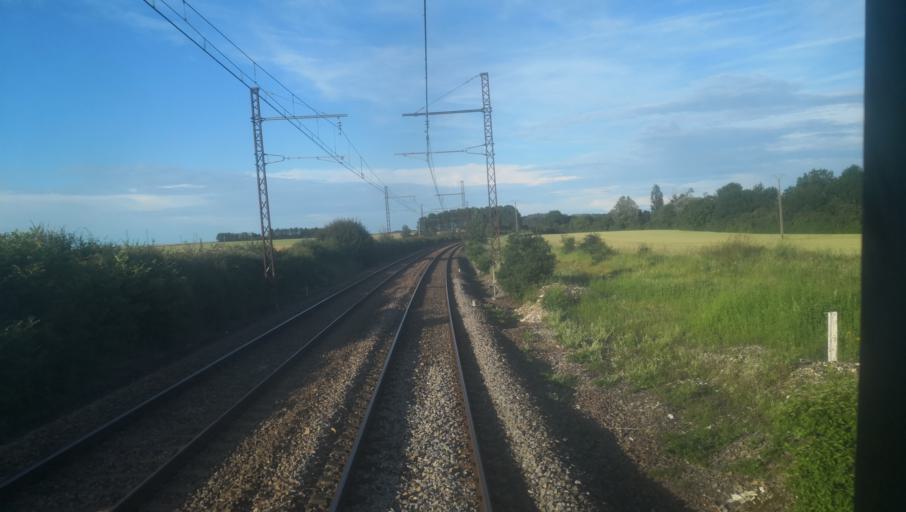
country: FR
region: Centre
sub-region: Departement de l'Indre
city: Neuvy-Pailloux
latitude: 46.9142
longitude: 1.9256
